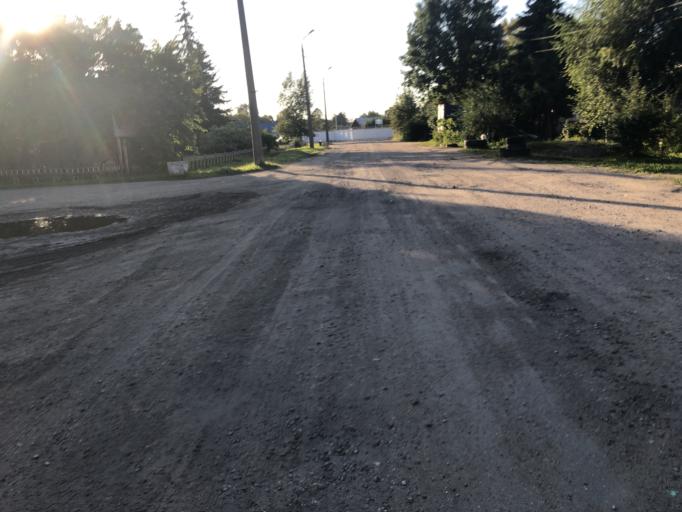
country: RU
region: Tverskaya
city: Rzhev
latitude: 56.2456
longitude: 34.3025
